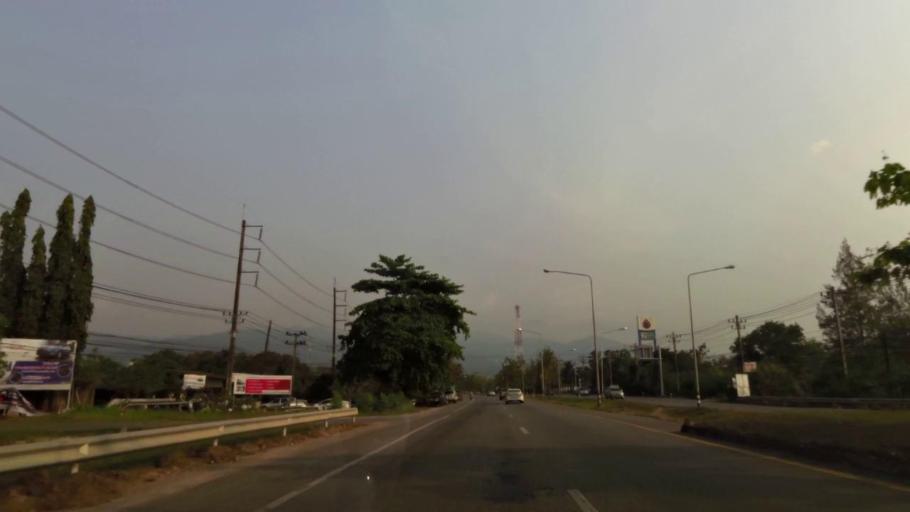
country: TH
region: Chanthaburi
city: Chanthaburi
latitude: 12.5969
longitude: 102.1420
